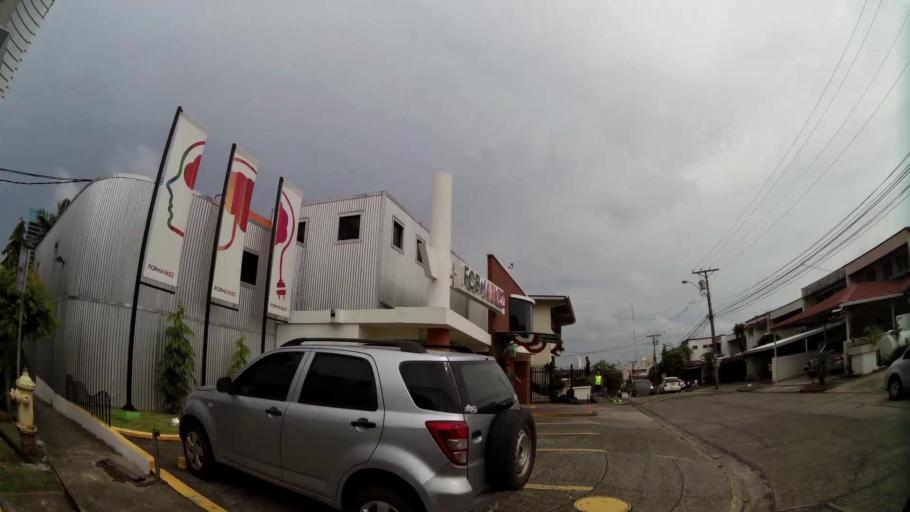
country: PA
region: Panama
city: Panama
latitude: 9.0002
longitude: -79.5322
